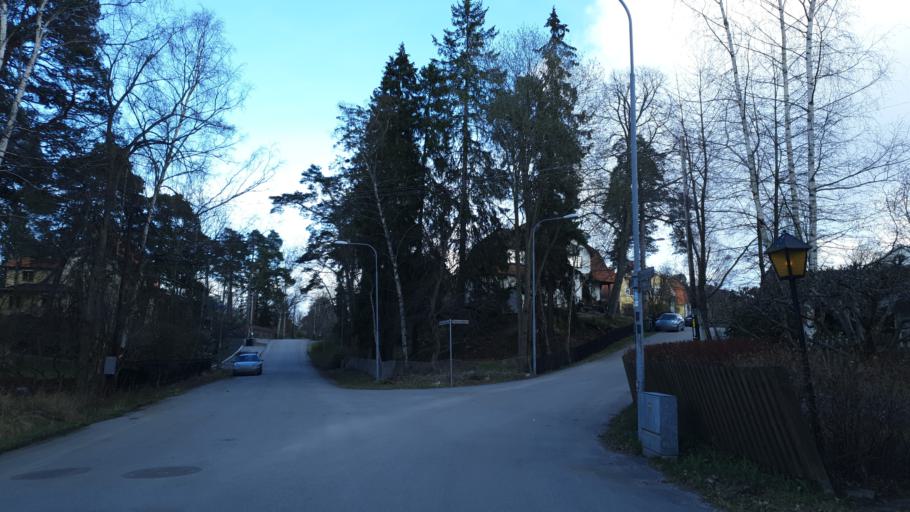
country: SE
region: Stockholm
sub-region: Lidingo
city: Lidingoe
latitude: 59.3701
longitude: 18.1398
